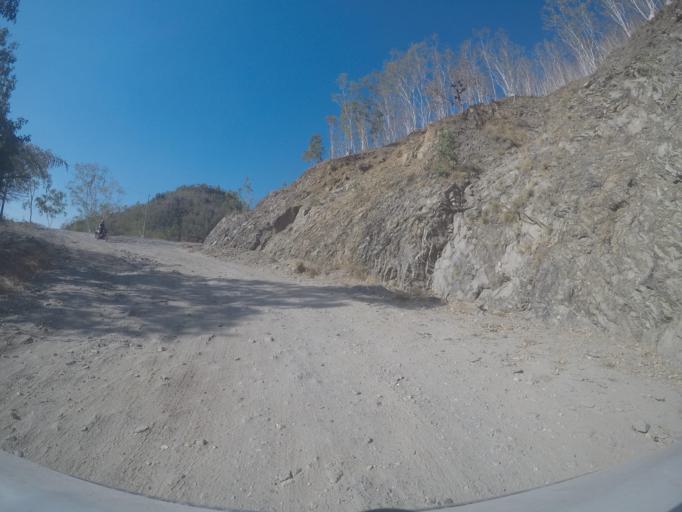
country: TL
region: Dili
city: Dili
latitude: -8.5338
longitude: 125.6173
